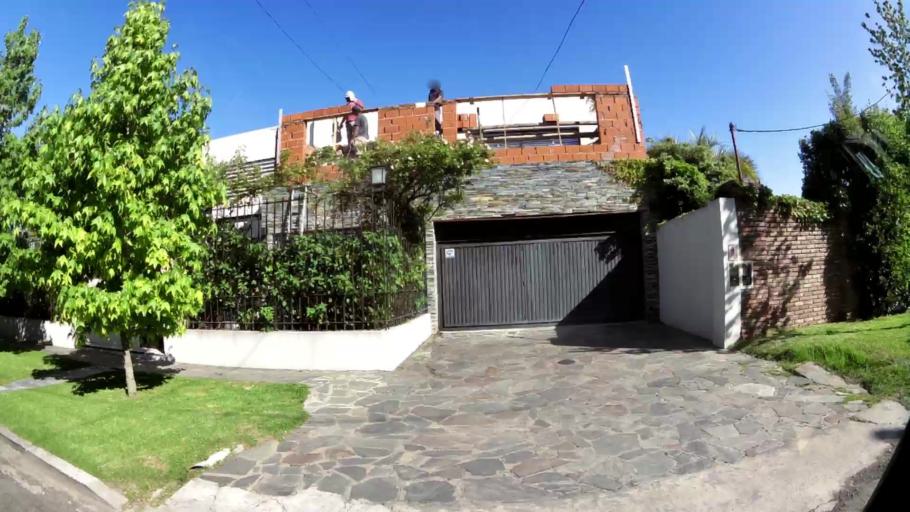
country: AR
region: Buenos Aires
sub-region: Partido de San Isidro
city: San Isidro
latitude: -34.4878
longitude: -58.5477
